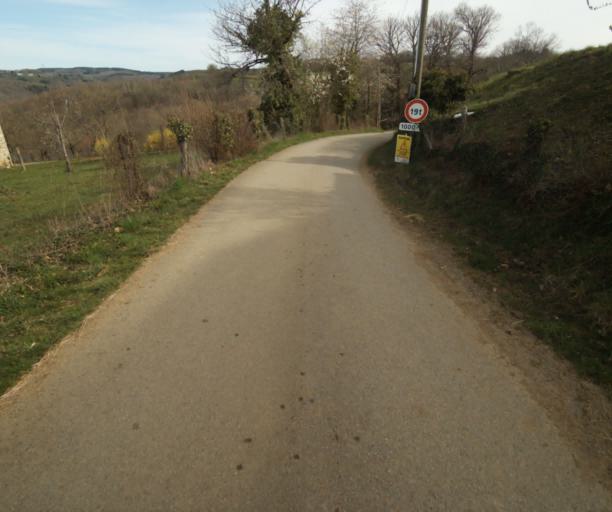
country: FR
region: Limousin
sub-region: Departement de la Correze
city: Correze
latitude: 45.4114
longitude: 1.8027
